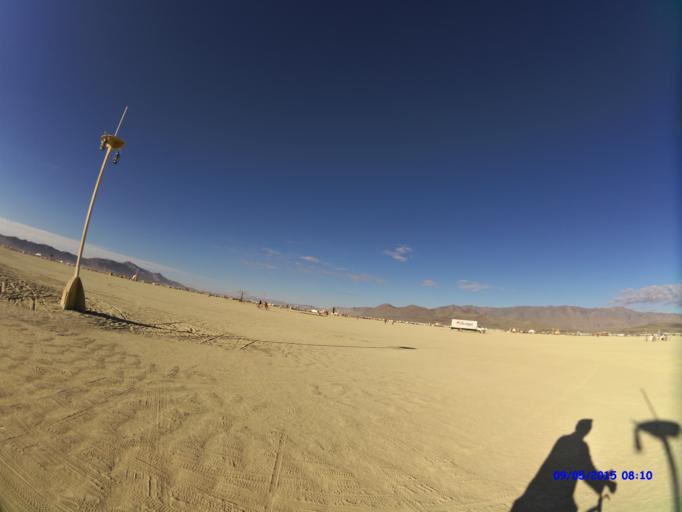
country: US
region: Nevada
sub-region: Pershing County
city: Lovelock
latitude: 40.7881
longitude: -119.2086
